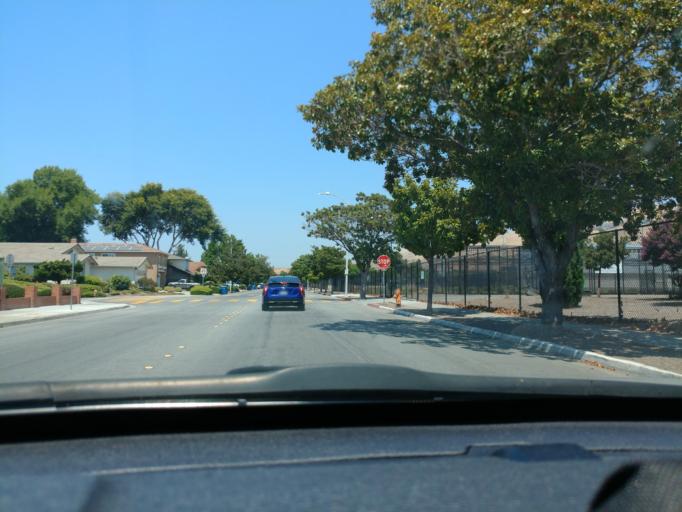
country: US
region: California
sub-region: Santa Clara County
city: Milpitas
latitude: 37.4487
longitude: -121.9046
